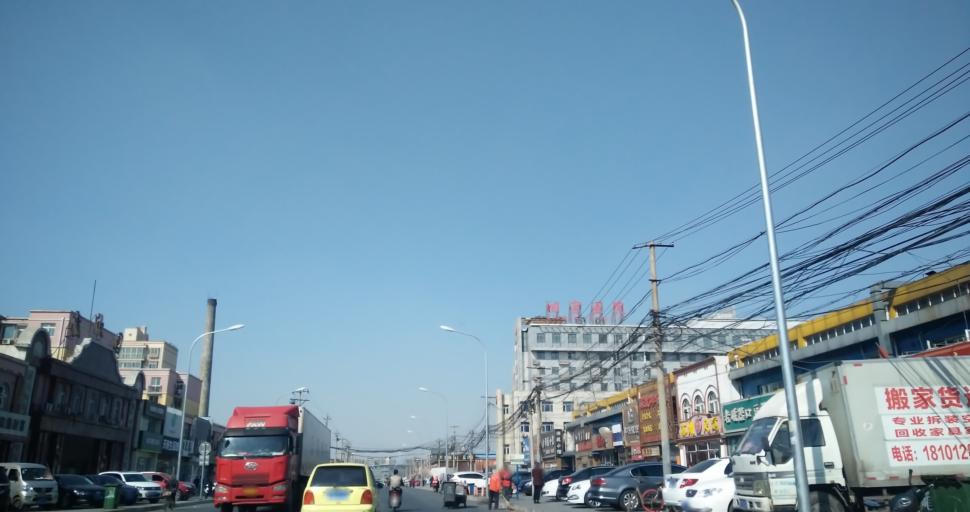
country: CN
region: Beijing
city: Jiugong
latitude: 39.8048
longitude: 116.4378
